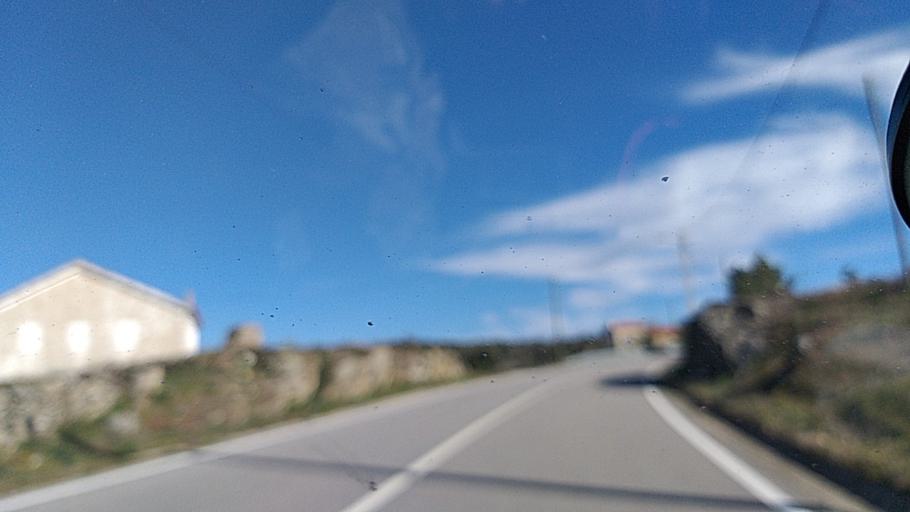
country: ES
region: Castille and Leon
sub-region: Provincia de Salamanca
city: Fuentes de Onoro
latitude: 40.6188
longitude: -6.8940
